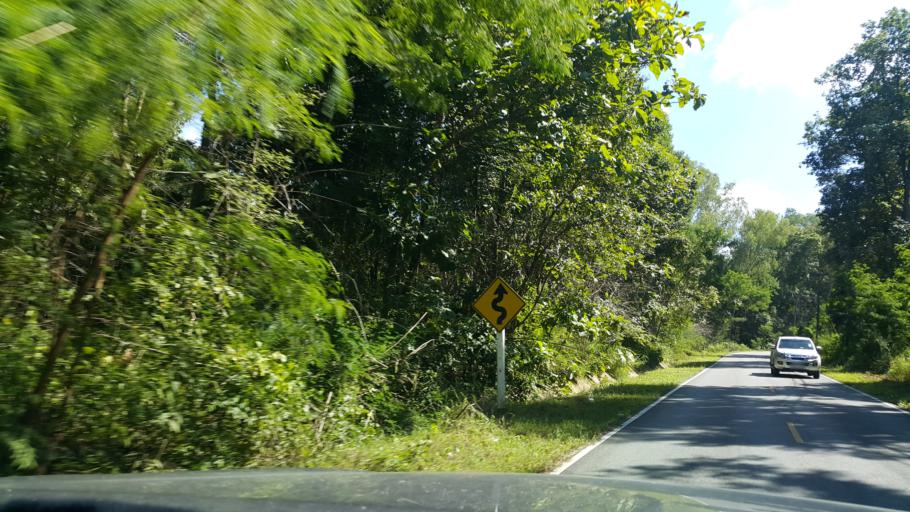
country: TH
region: Chiang Mai
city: Mae On
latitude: 18.7326
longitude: 99.2661
